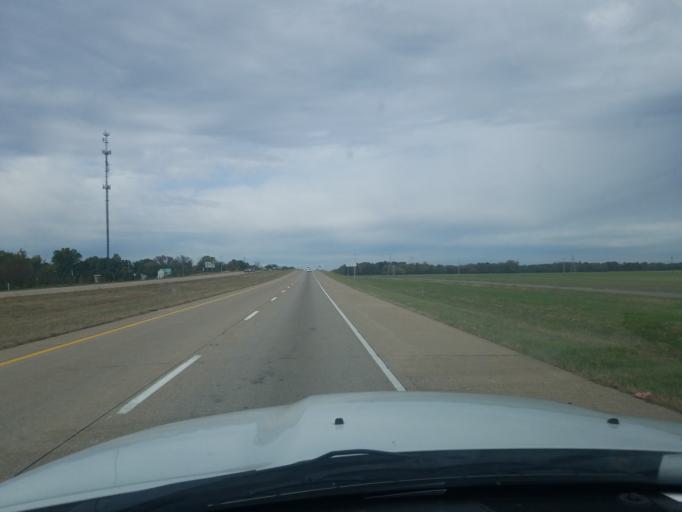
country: US
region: Indiana
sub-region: Vanderburgh County
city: Melody Hill
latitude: 38.0239
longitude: -87.4712
